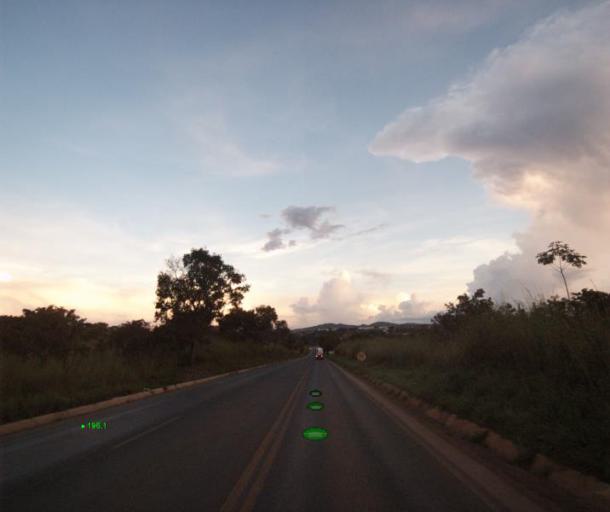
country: BR
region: Goias
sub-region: Uruacu
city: Uruacu
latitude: -14.4938
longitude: -49.1521
